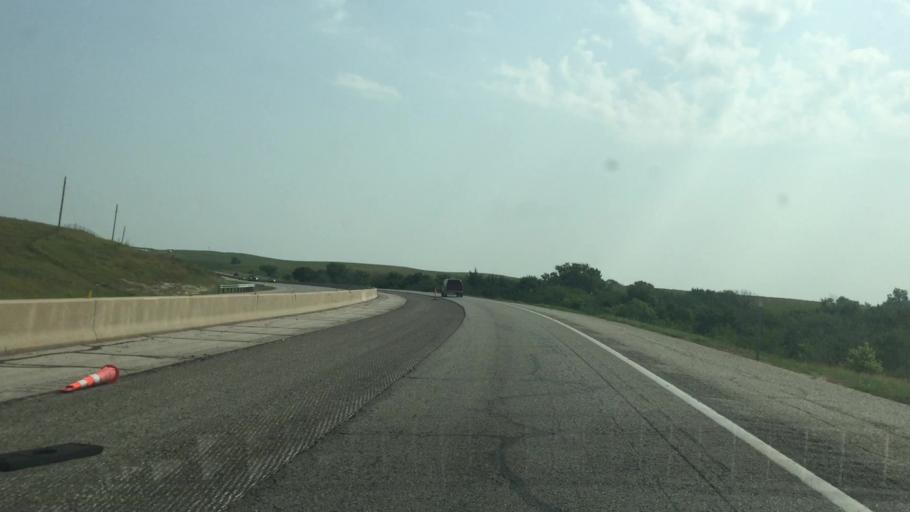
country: US
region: Kansas
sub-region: Chase County
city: Cottonwood Falls
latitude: 38.1499
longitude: -96.4955
